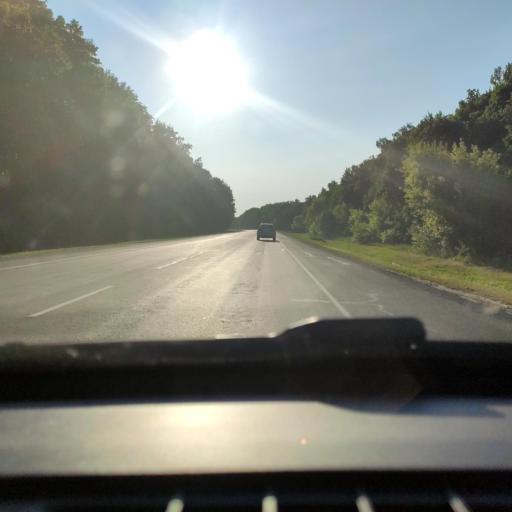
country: RU
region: Voronezj
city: Kashirskoye
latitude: 51.4882
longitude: 39.6414
